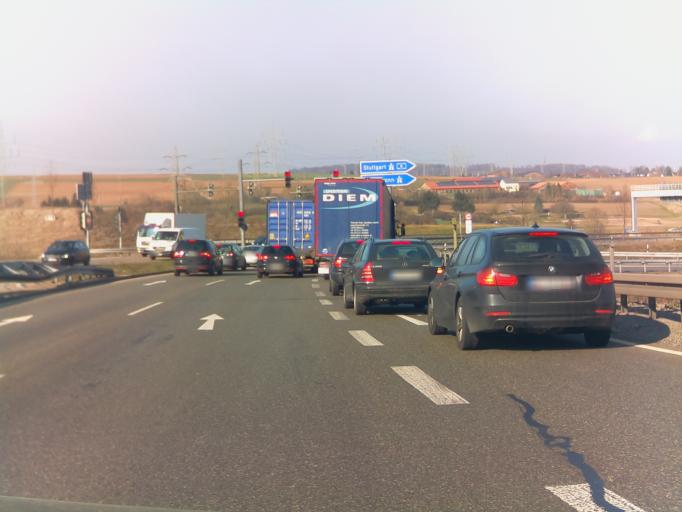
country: DE
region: Baden-Wuerttemberg
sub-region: Regierungsbezirk Stuttgart
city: Leonberg
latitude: 48.7868
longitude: 8.9805
